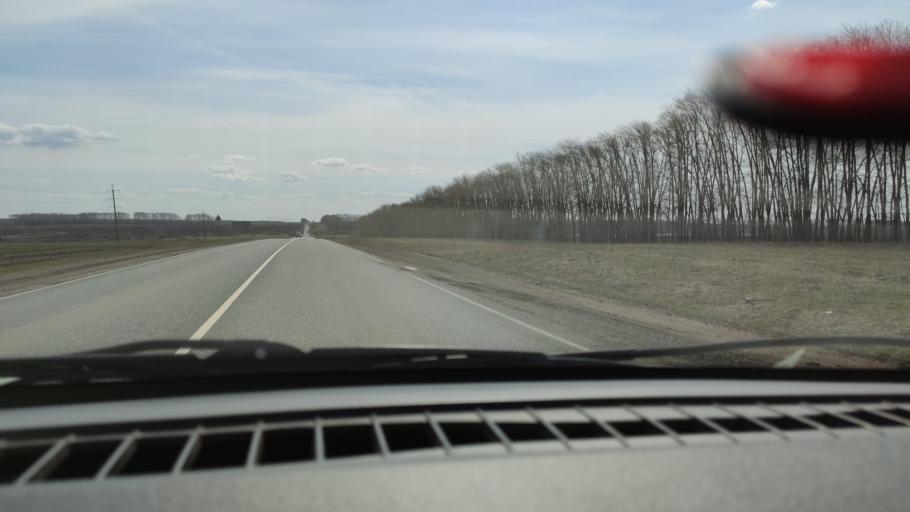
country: RU
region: Bashkortostan
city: Dyurtyuli
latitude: 55.2593
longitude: 55.0621
